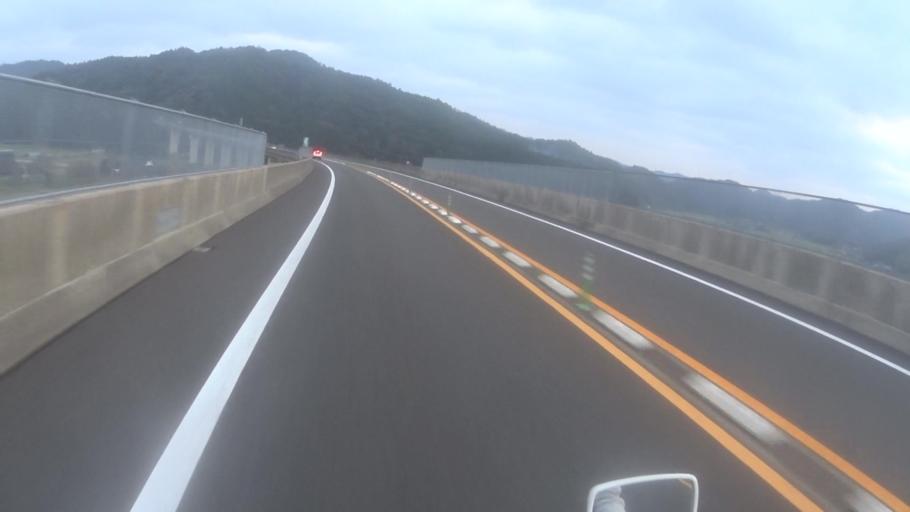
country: JP
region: Kyoto
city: Ayabe
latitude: 35.3877
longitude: 135.2413
